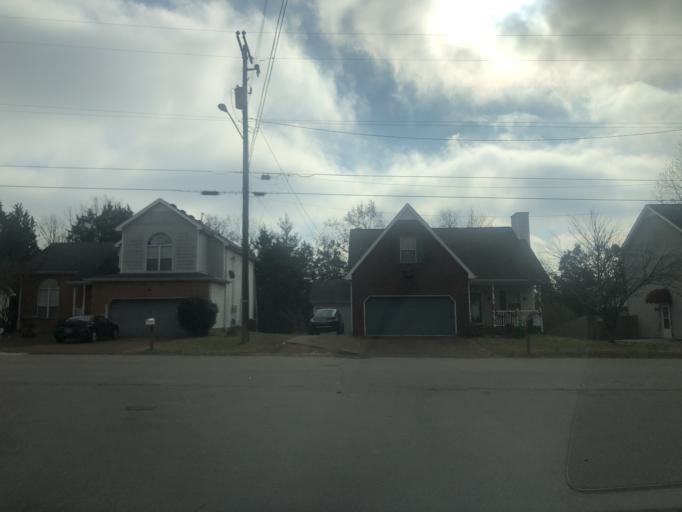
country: US
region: Tennessee
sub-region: Rutherford County
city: La Vergne
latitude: 36.0792
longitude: -86.6511
